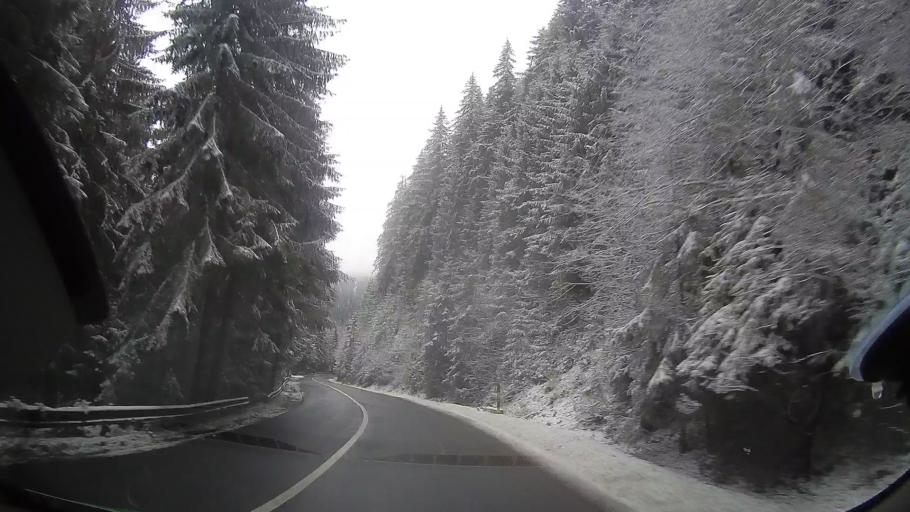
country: RO
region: Cluj
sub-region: Comuna Belis
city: Belis
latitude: 46.6513
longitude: 23.0491
